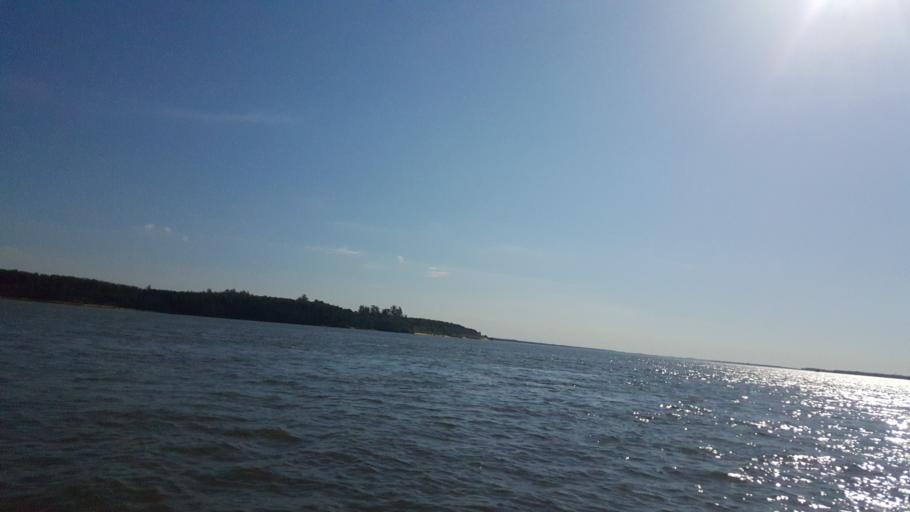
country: AR
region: Corrientes
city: Ituzaingo
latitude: -27.6031
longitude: -56.8525
